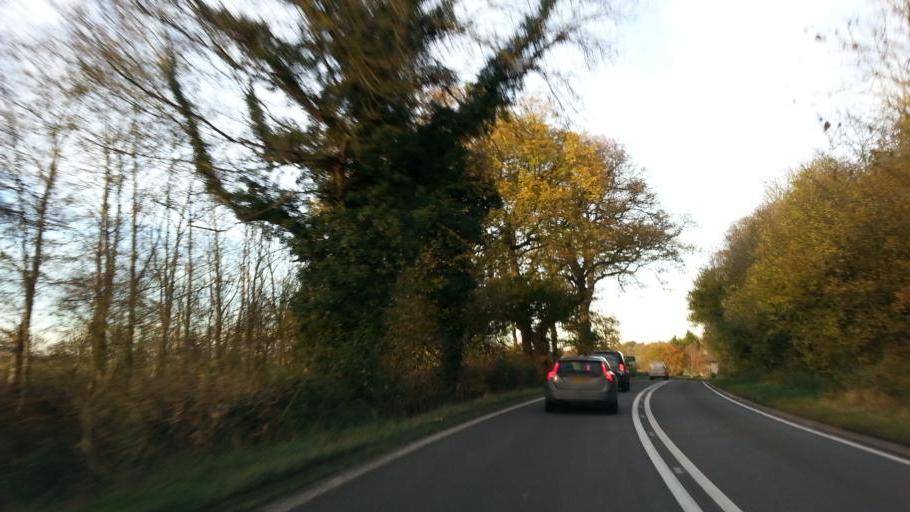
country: GB
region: England
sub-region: District of Rutland
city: Morcott
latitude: 52.5223
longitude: -0.5920
